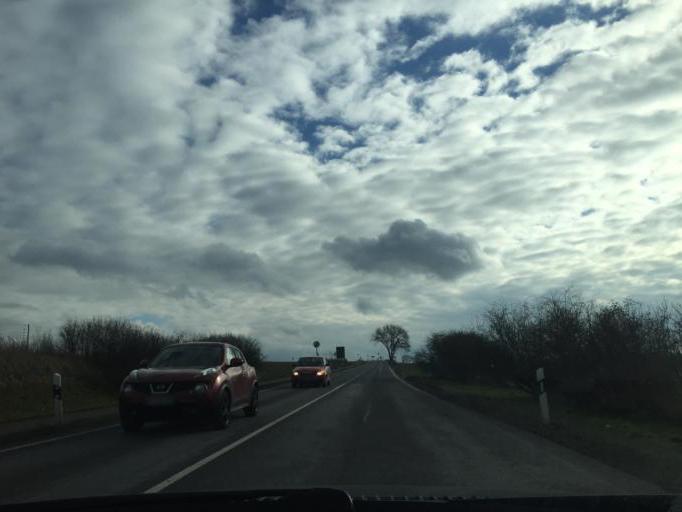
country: DE
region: Saxony
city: Ottendorf-Okrilla
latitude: 51.1699
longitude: 13.8596
